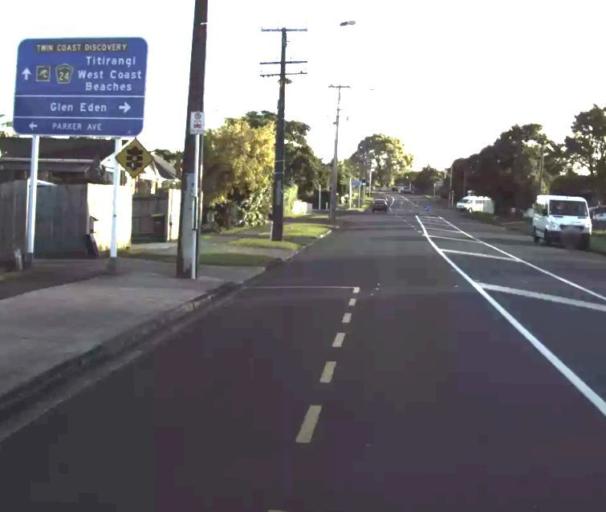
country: NZ
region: Auckland
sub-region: Auckland
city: Waitakere
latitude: -36.9162
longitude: 174.6685
